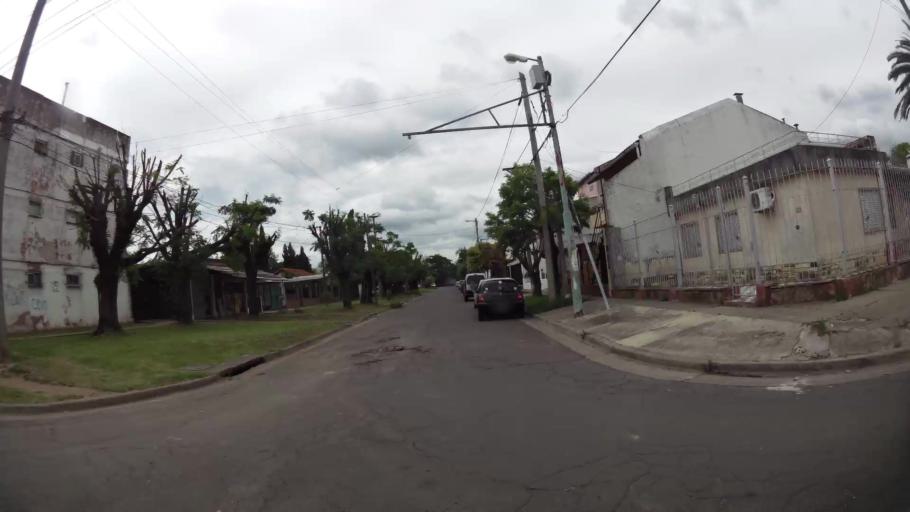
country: AR
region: Buenos Aires
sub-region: Partido de Zarate
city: Zarate
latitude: -34.1158
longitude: -59.0178
